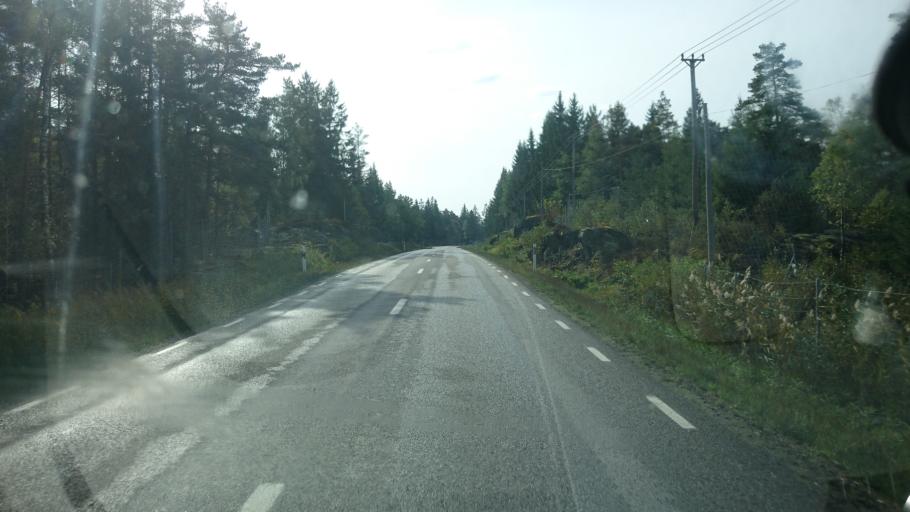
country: SE
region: Vaestra Goetaland
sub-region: Alingsas Kommun
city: Sollebrunn
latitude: 58.1948
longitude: 12.4313
